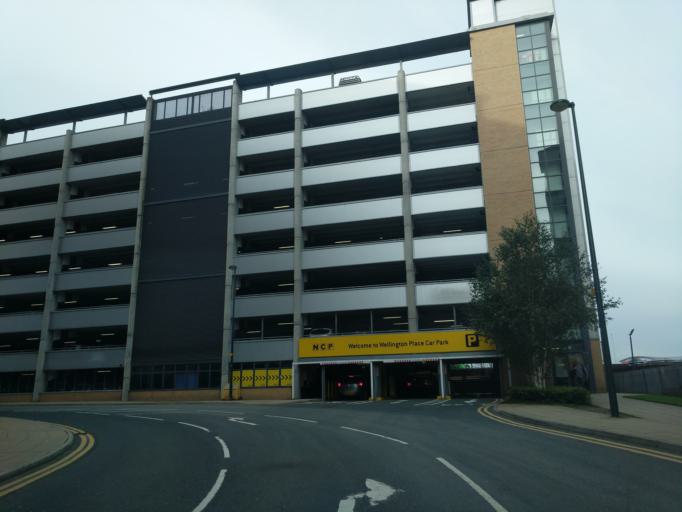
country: GB
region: England
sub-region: City and Borough of Leeds
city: Leeds
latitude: 53.7964
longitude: -1.5581
